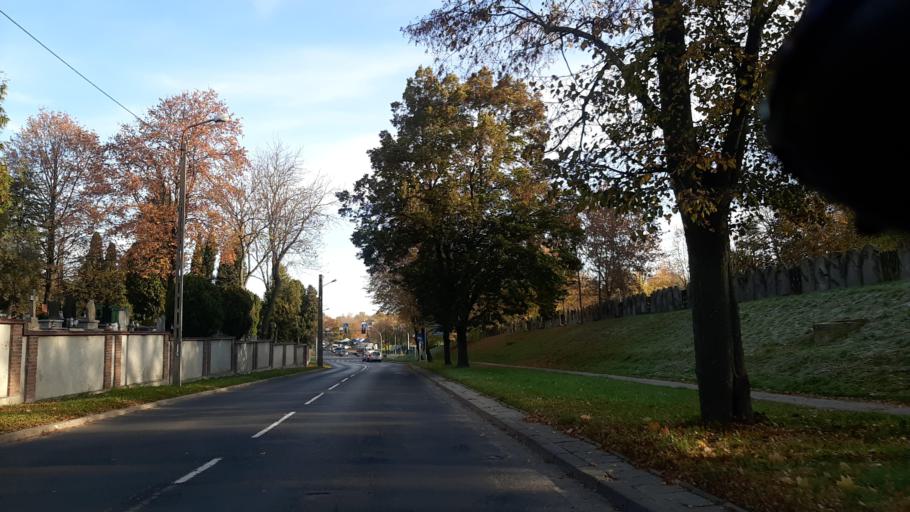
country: PL
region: Lublin Voivodeship
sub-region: Powiat lubelski
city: Lublin
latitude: 51.2582
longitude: 22.5778
